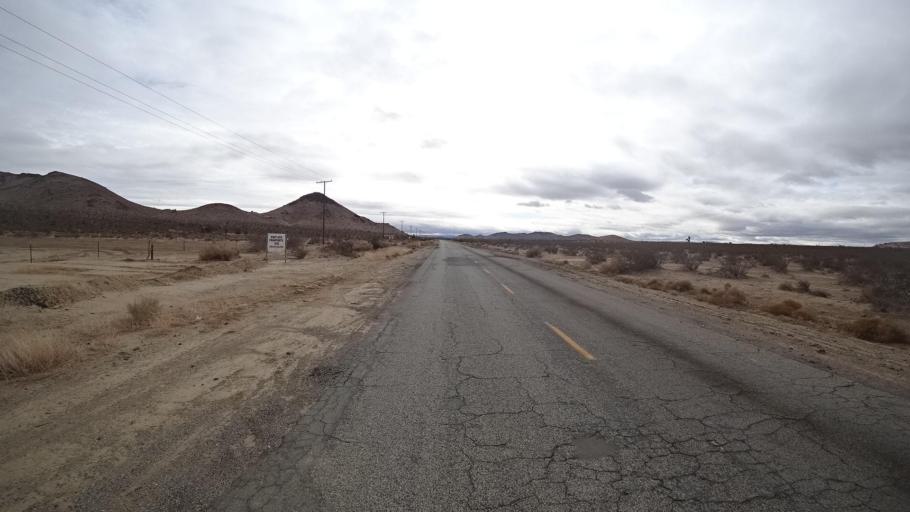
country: US
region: California
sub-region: Kern County
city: Mojave
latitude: 34.9767
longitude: -118.2098
